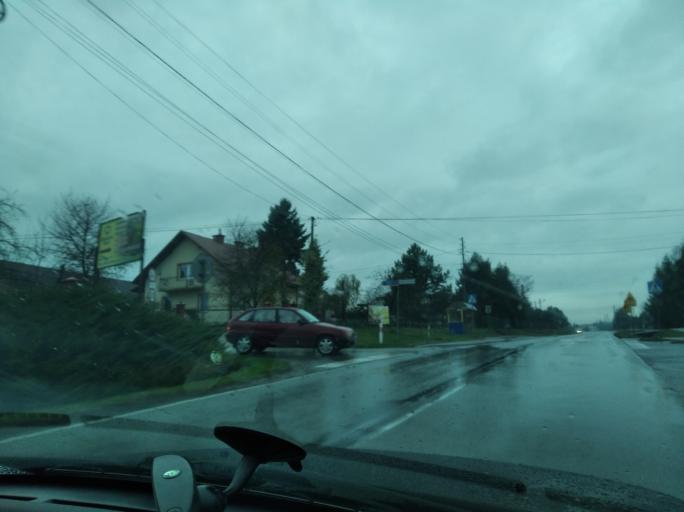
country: PL
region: Subcarpathian Voivodeship
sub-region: Powiat lancucki
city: Lancut
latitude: 50.0419
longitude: 22.2287
